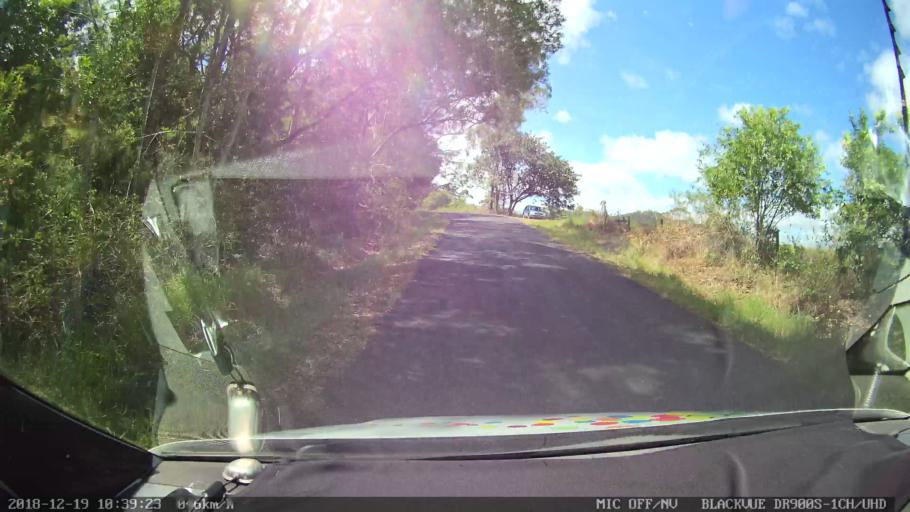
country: AU
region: New South Wales
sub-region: Lismore Municipality
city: Nimbin
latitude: -28.5803
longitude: 153.1546
